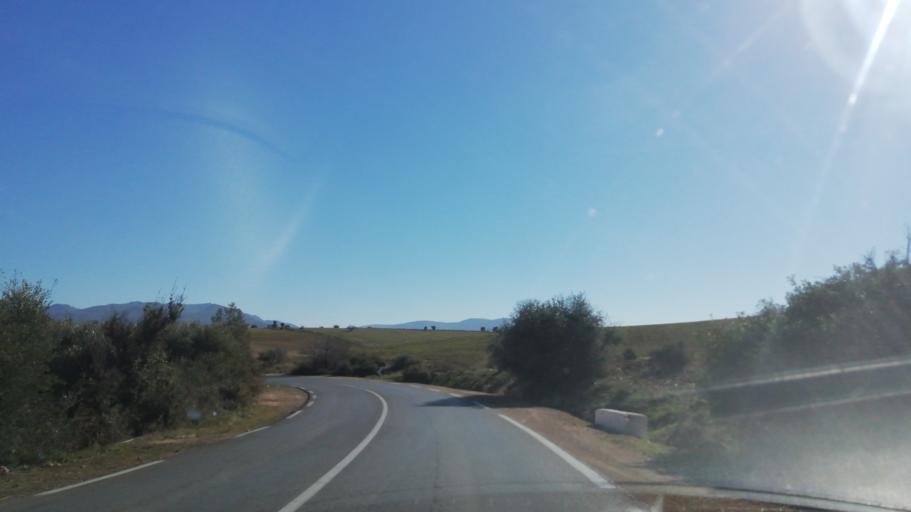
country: DZ
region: Tlemcen
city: Beni Mester
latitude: 34.8257
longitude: -1.5859
